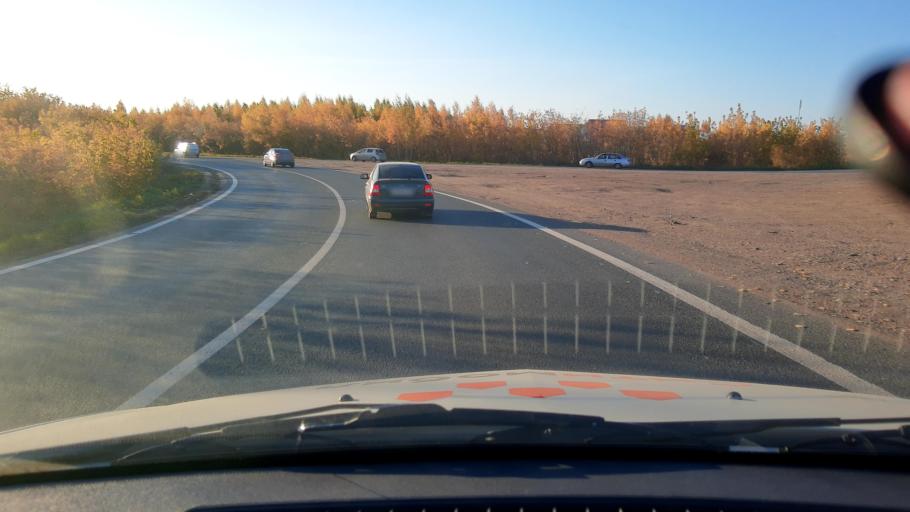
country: RU
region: Bashkortostan
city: Iglino
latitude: 54.7757
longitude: 56.2554
